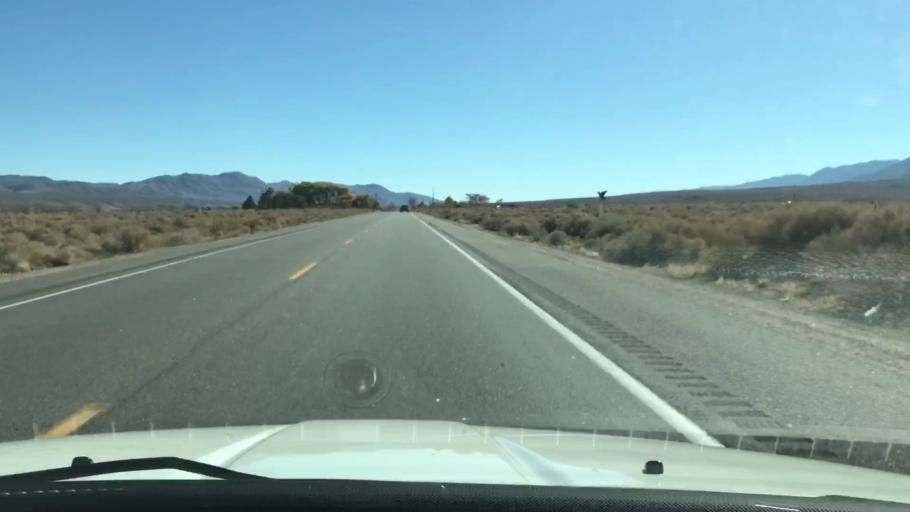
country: US
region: California
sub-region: Inyo County
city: Lone Pine
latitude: 36.2628
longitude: -117.9968
